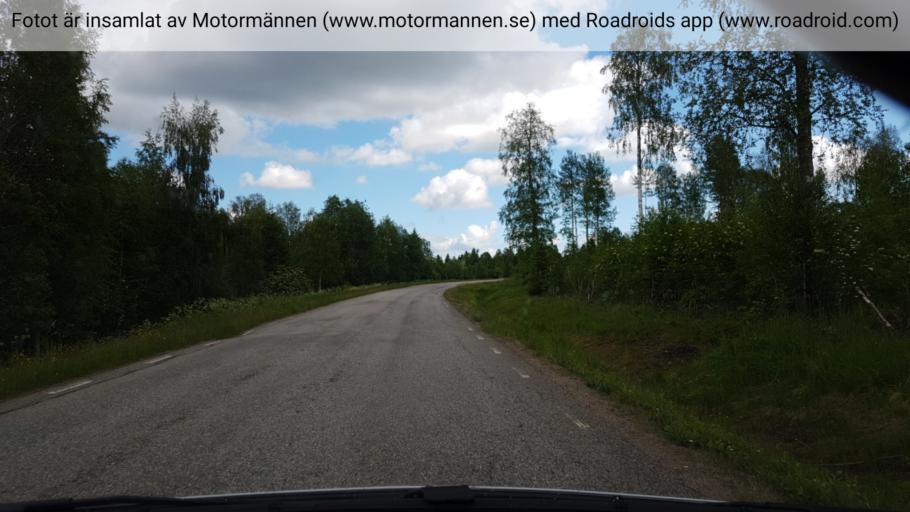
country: FI
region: Lapland
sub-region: Torniolaakso
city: Ylitornio
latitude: 66.1863
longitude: 23.7408
